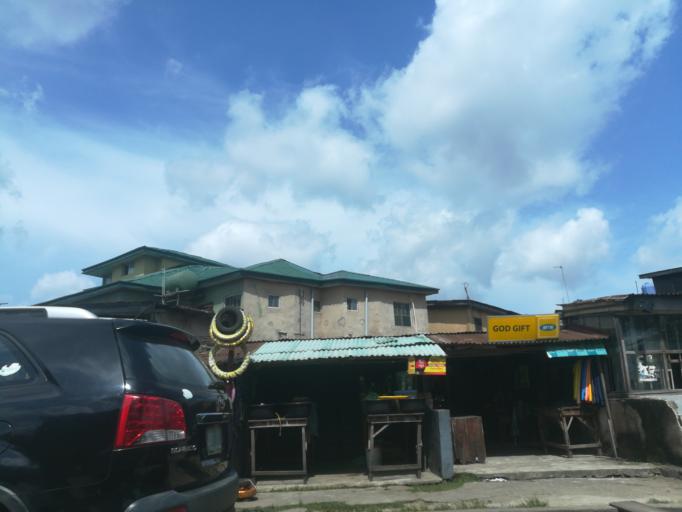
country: NG
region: Lagos
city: Somolu
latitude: 6.5286
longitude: 3.3807
